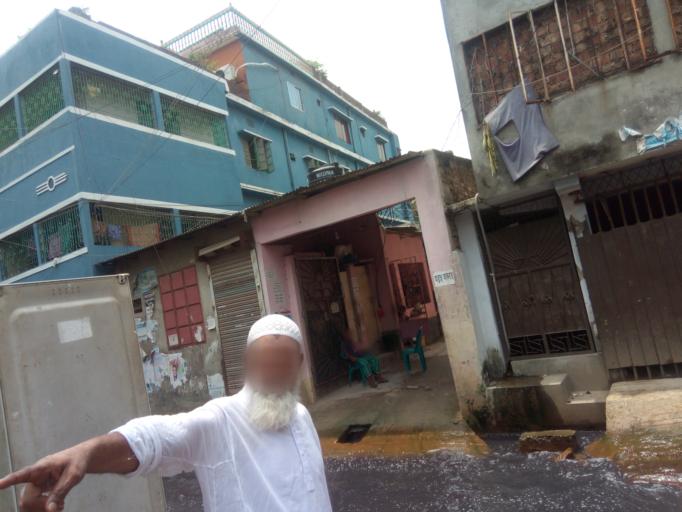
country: BD
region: Dhaka
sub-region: Dhaka
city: Dhaka
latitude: 23.6917
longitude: 90.4384
